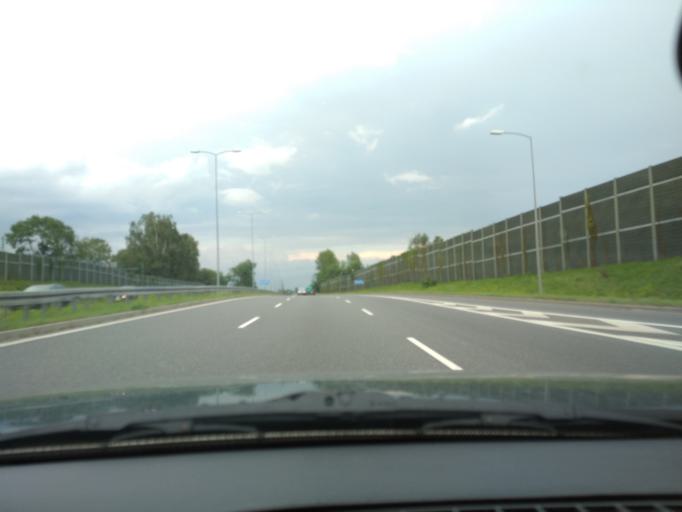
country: PL
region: Silesian Voivodeship
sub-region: Zabrze
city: Zabrze
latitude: 50.2929
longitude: 18.8174
